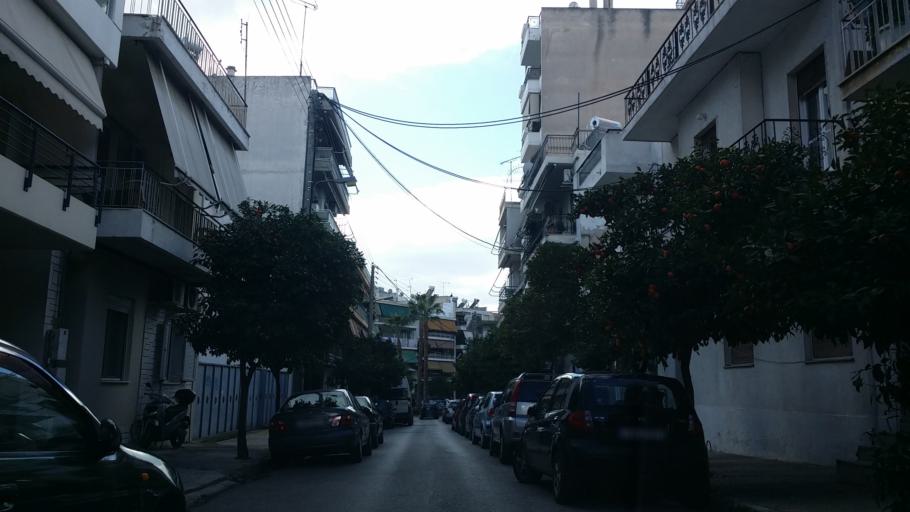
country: GR
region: Attica
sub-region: Nomos Piraios
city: Korydallos
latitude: 37.9788
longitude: 23.6469
